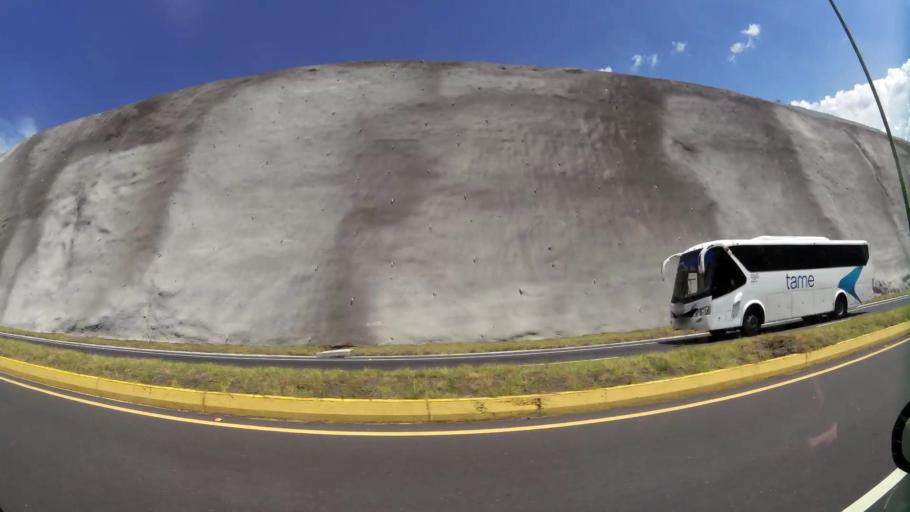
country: EC
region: Pichincha
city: Quito
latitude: -0.1009
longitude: -78.3826
